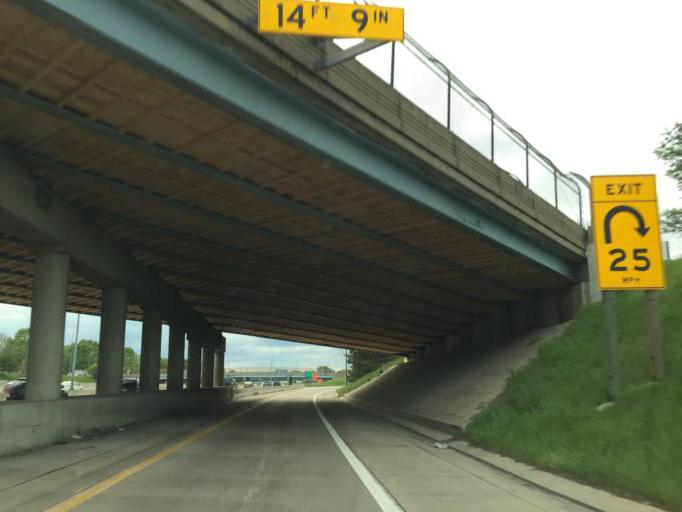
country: US
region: Michigan
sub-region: Wayne County
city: Dearborn Heights
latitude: 42.3805
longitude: -83.2363
